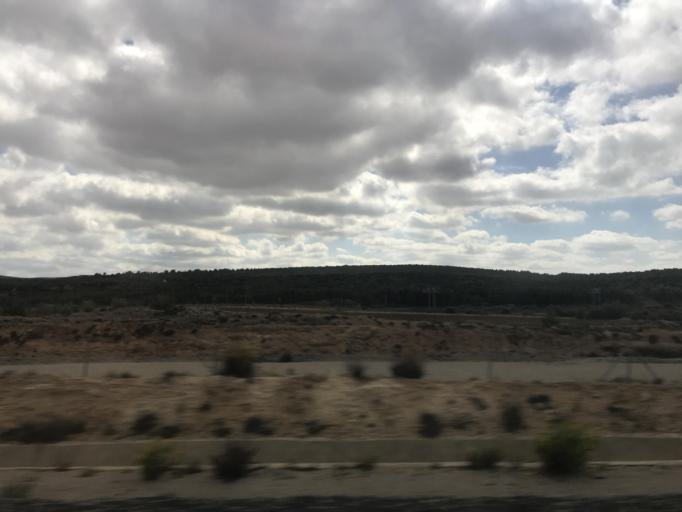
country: ES
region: Castille-La Mancha
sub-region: Provincia de Albacete
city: Almansa
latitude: 38.8750
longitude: -1.1683
